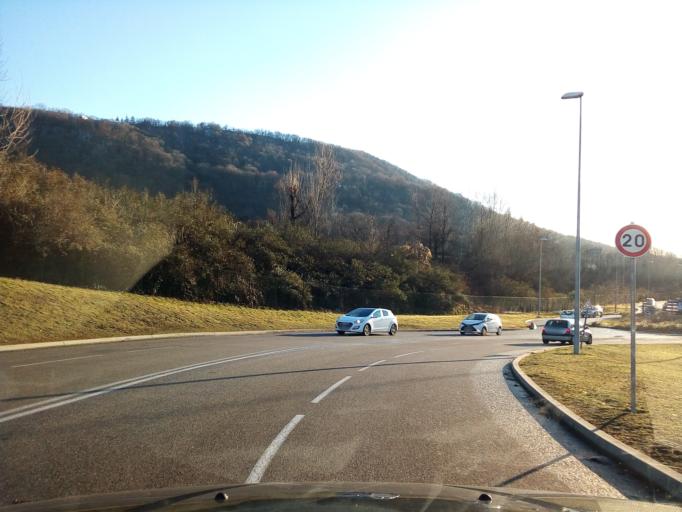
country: FR
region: Rhone-Alpes
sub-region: Departement de l'Isere
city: Gieres
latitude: 45.1817
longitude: 5.7773
